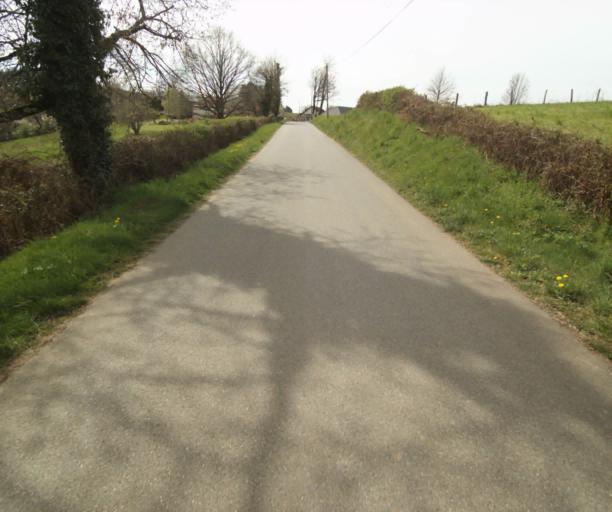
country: FR
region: Limousin
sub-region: Departement de la Correze
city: Naves
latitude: 45.3035
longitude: 1.7646
